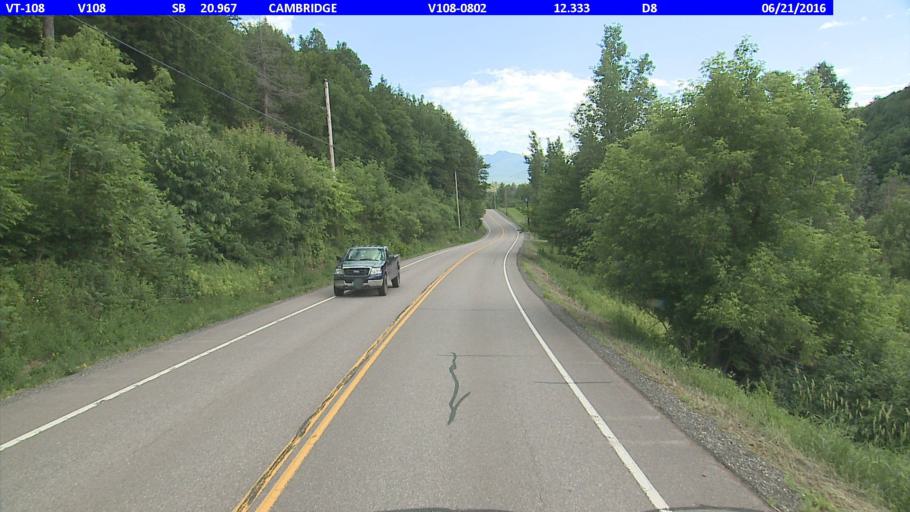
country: US
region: Vermont
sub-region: Lamoille County
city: Johnson
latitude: 44.6930
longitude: -72.8272
